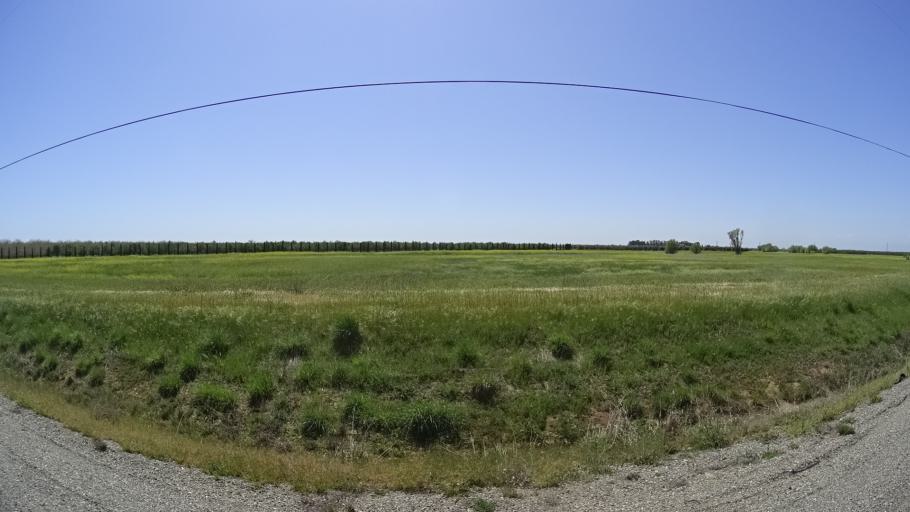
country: US
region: California
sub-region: Glenn County
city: Hamilton City
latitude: 39.7668
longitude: -122.0389
